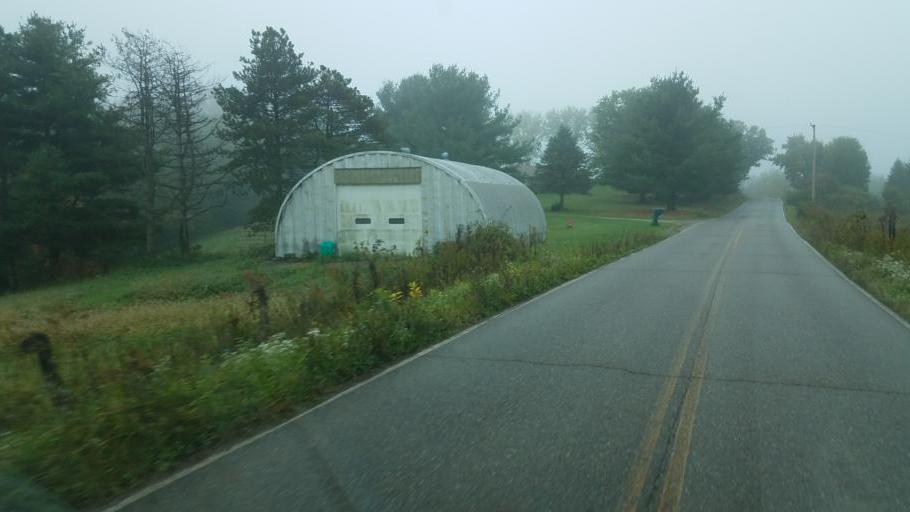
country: US
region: Ohio
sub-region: Harrison County
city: Cadiz
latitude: 40.3814
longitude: -81.1095
